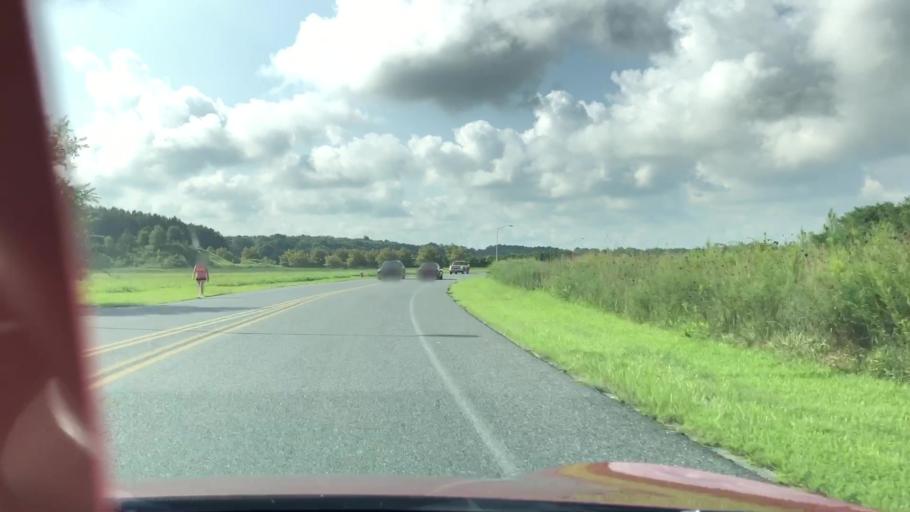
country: US
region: Maryland
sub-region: Wicomico County
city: Delmar
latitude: 38.4063
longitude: -75.5628
